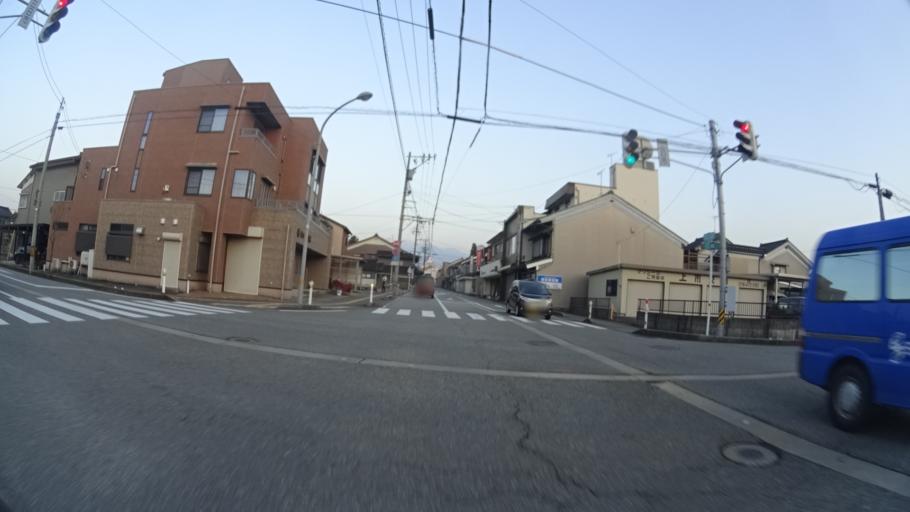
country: JP
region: Toyama
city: Kamiichi
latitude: 36.7065
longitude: 137.3589
